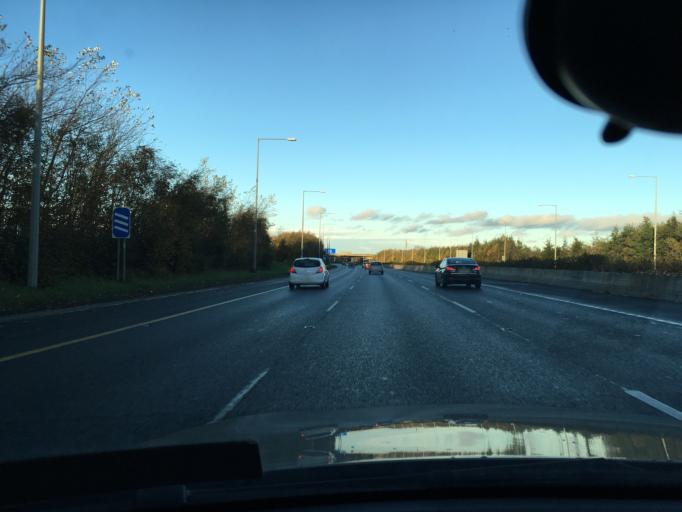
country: IE
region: Leinster
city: Kinsealy-Drinan
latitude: 53.4356
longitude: -6.2110
